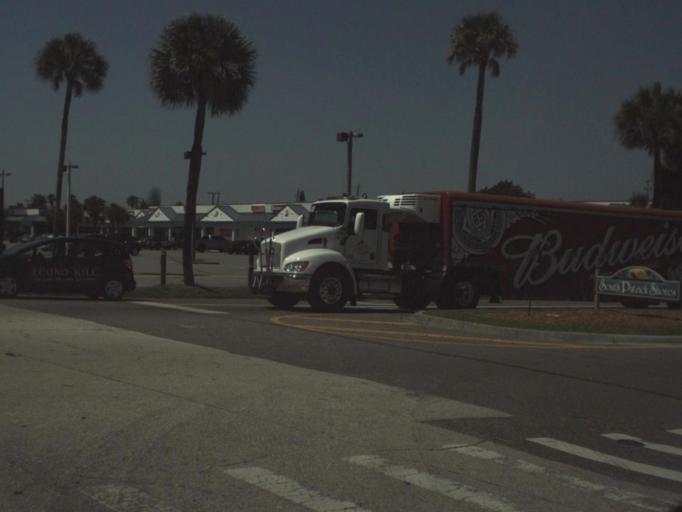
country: US
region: Florida
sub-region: Brevard County
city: South Patrick Shores
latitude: 28.2086
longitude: -80.5973
